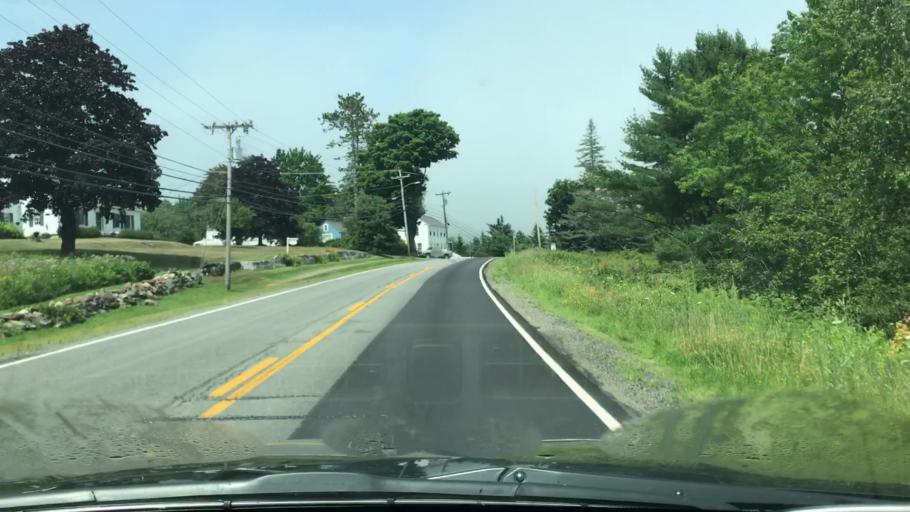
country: US
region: Maine
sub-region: Waldo County
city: Lincolnville
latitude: 44.2941
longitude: -69.0077
